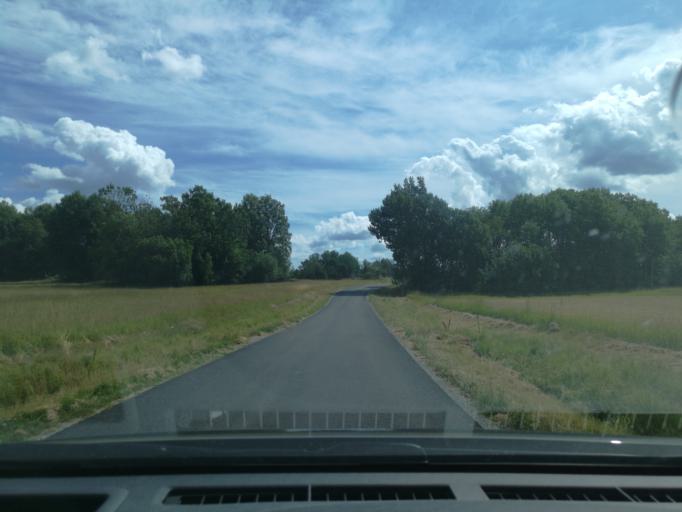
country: SE
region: Stockholm
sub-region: Sigtuna Kommun
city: Marsta
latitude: 59.6508
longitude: 17.8822
